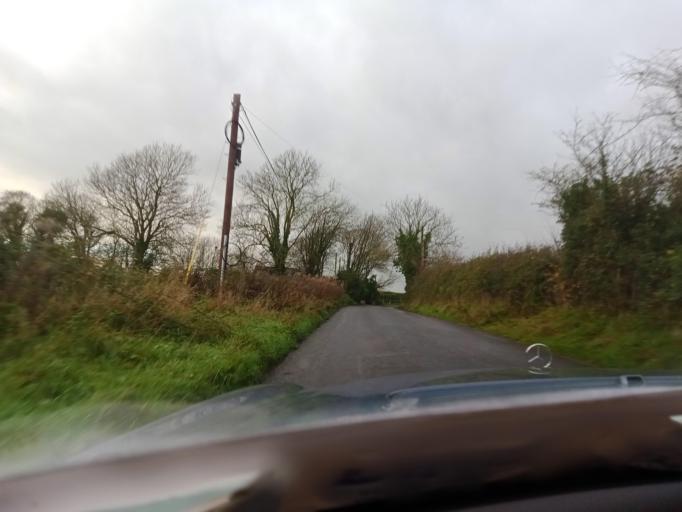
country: IE
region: Munster
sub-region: Waterford
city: Waterford
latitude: 52.2774
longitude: -7.1747
